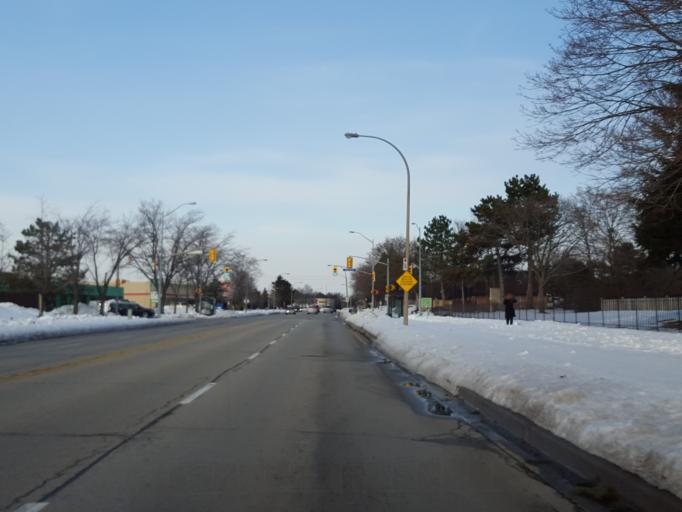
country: CA
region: Ontario
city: Burlington
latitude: 43.3482
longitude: -79.7908
